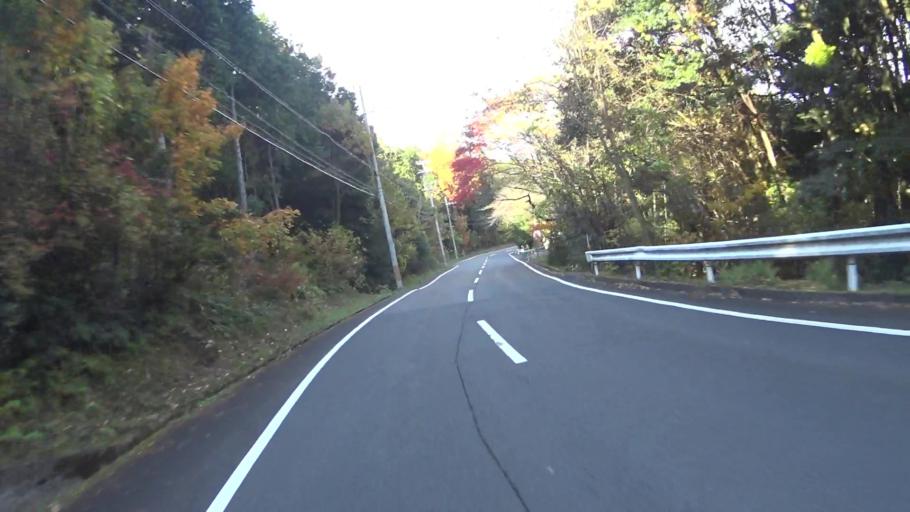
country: JP
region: Kyoto
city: Maizuru
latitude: 35.5458
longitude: 135.3959
